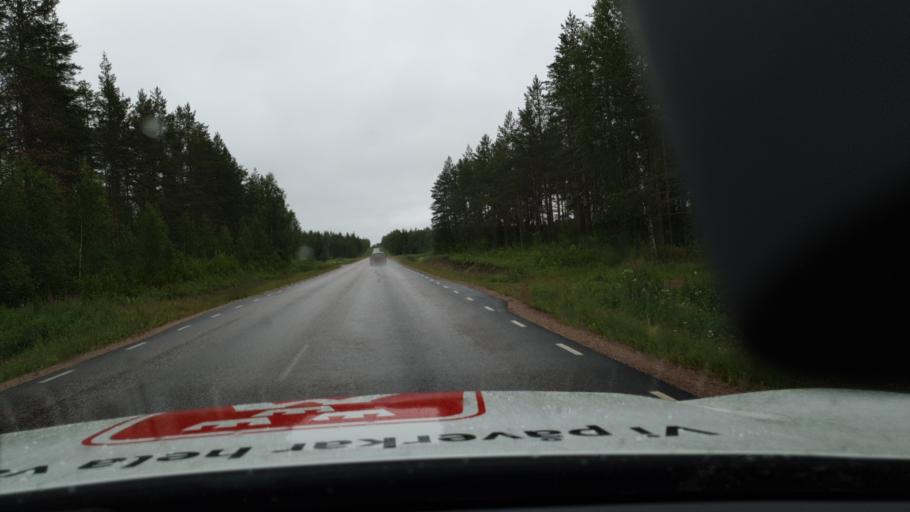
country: SE
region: Norrbotten
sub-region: Overtornea Kommun
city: OEvertornea
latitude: 66.5186
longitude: 23.7501
